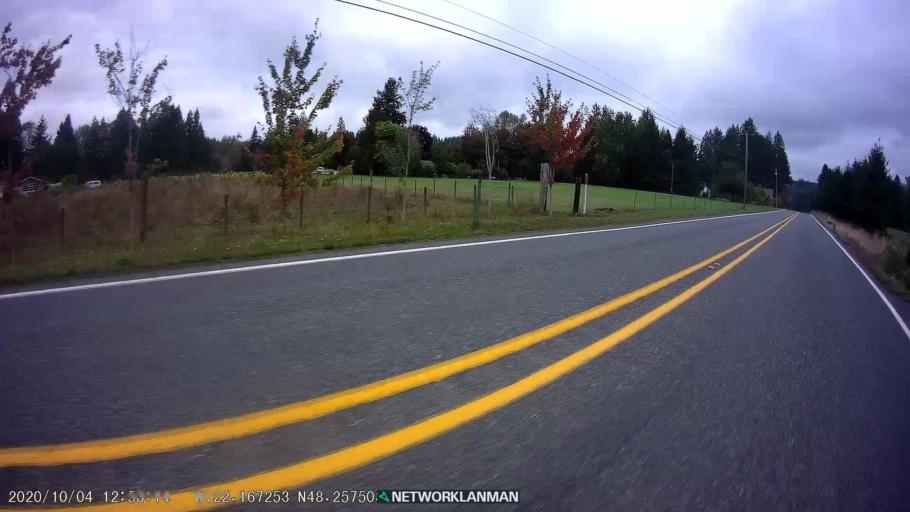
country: US
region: Washington
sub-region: Snohomish County
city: Bryant
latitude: 48.2575
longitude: -122.1661
